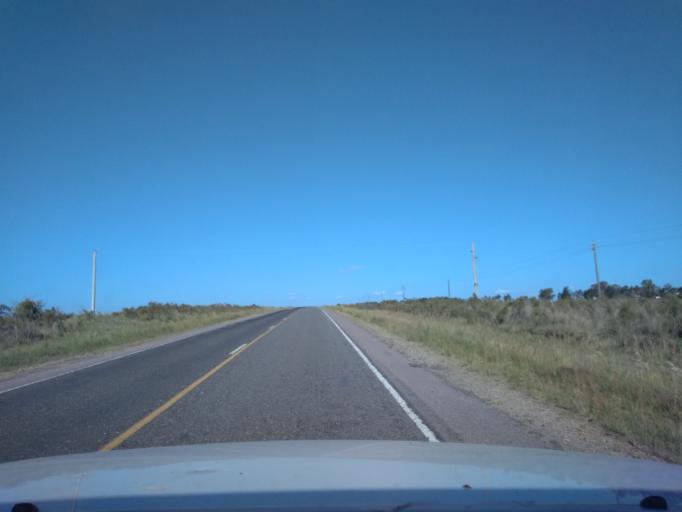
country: UY
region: Canelones
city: San Ramon
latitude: -34.0416
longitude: -55.9490
